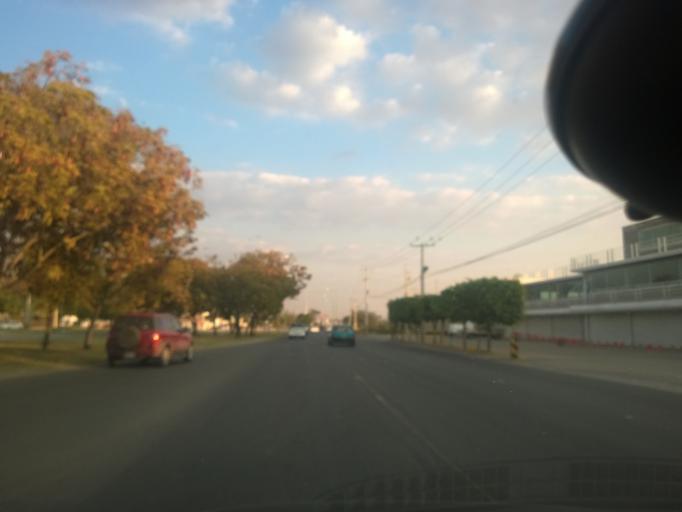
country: MX
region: Guanajuato
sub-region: Leon
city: Medina
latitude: 21.1574
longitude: -101.6428
